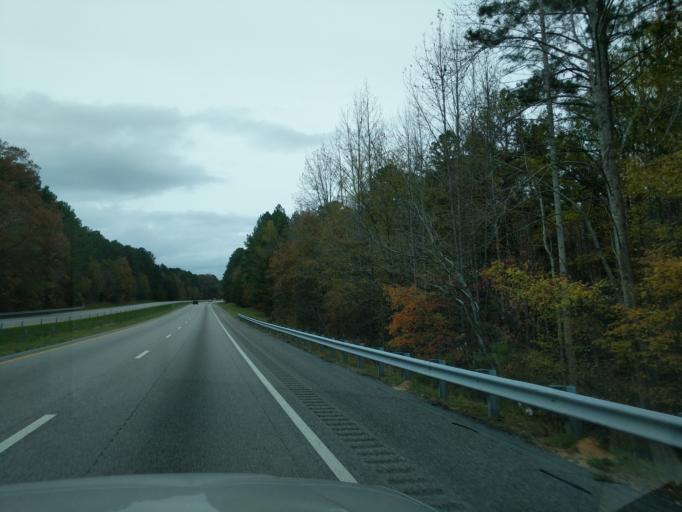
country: US
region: South Carolina
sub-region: Laurens County
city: Clinton
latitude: 34.5253
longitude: -81.8786
